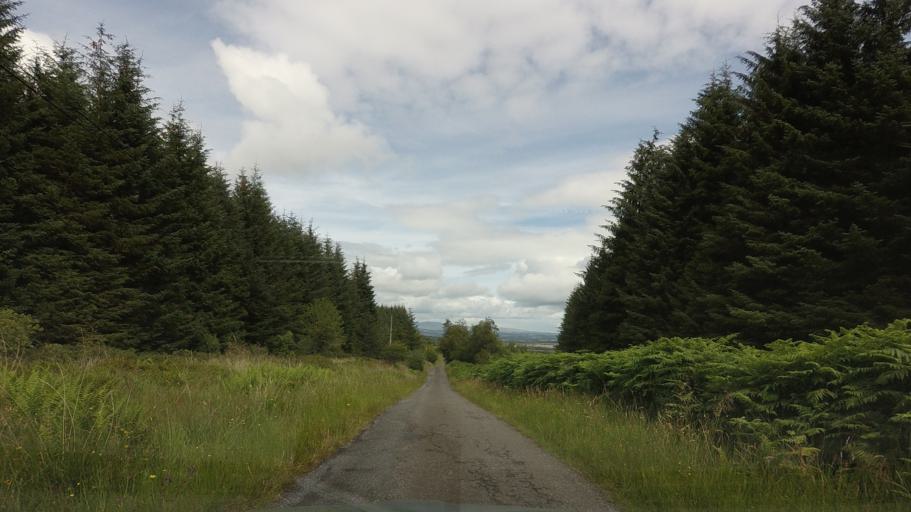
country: GB
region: Scotland
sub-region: Stirling
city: Killearn
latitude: 56.1087
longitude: -4.4091
